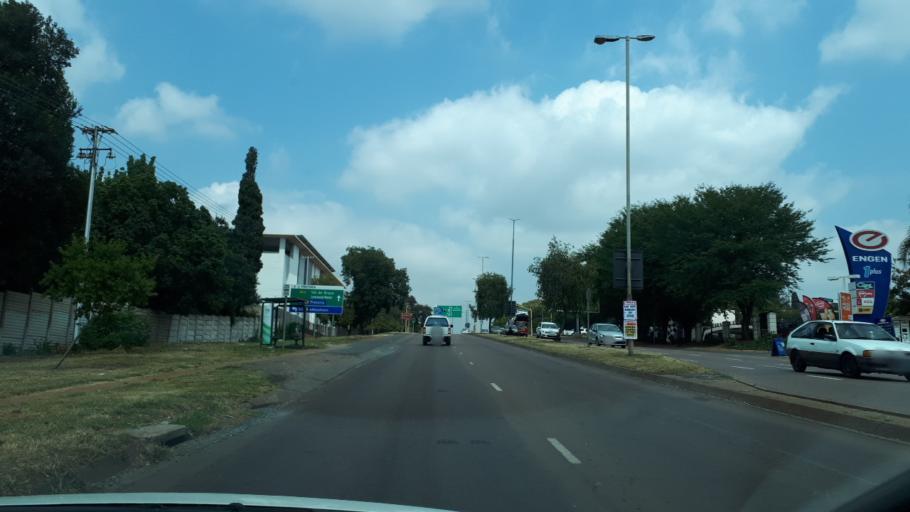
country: ZA
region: Gauteng
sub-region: City of Tshwane Metropolitan Municipality
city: Pretoria
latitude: -25.7444
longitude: 28.2957
